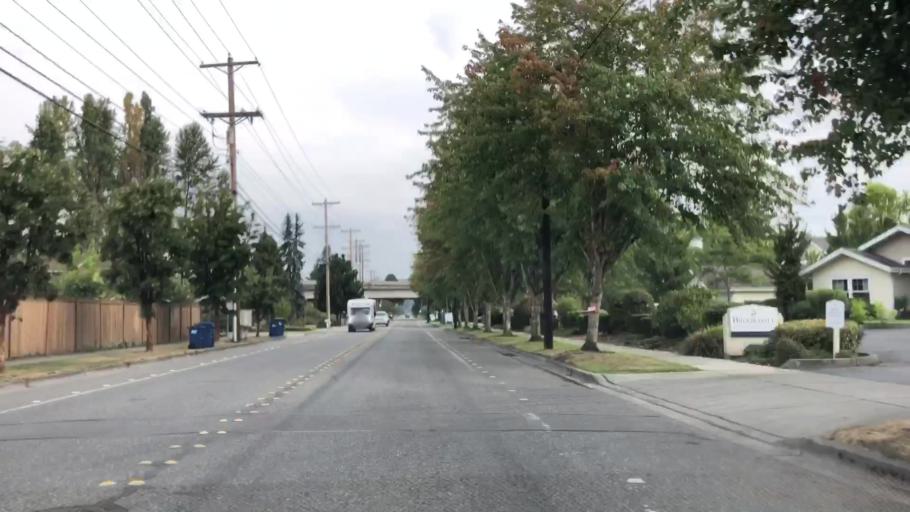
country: US
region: Washington
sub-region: Snohomish County
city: Monroe
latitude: 47.8558
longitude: -121.9906
